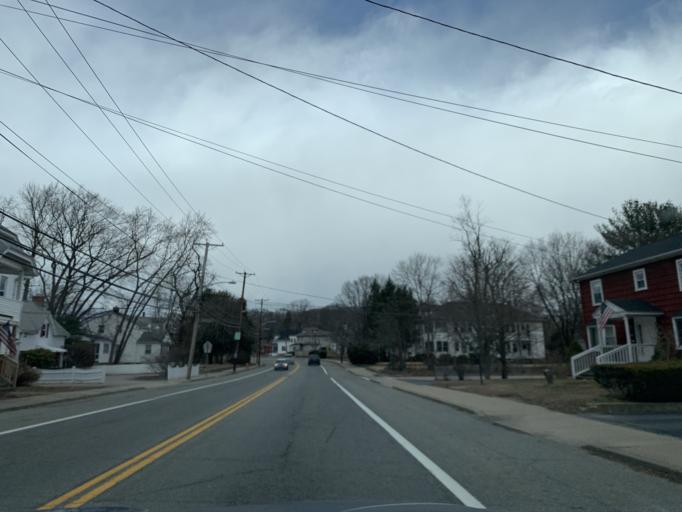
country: US
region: Rhode Island
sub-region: Providence County
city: Cumberland Hill
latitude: 42.0059
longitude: -71.4778
